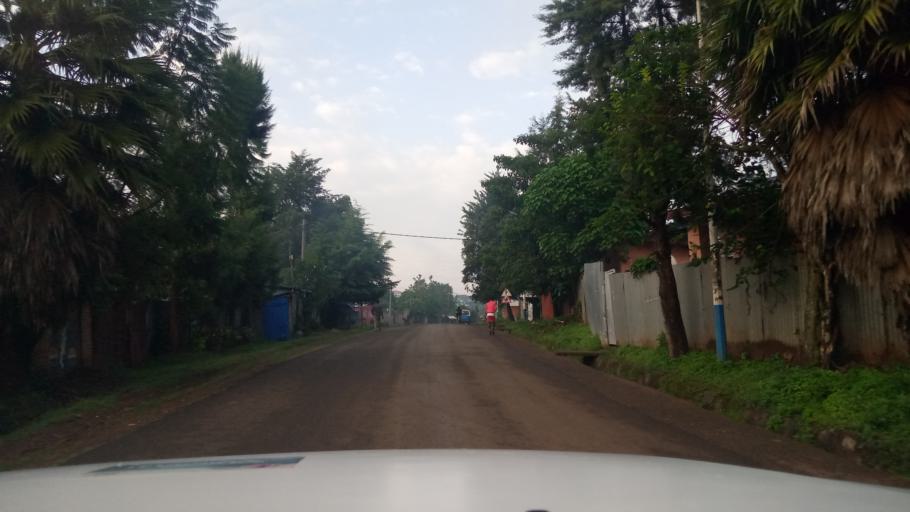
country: ET
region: Oromiya
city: Jima
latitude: 7.6783
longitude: 36.8401
